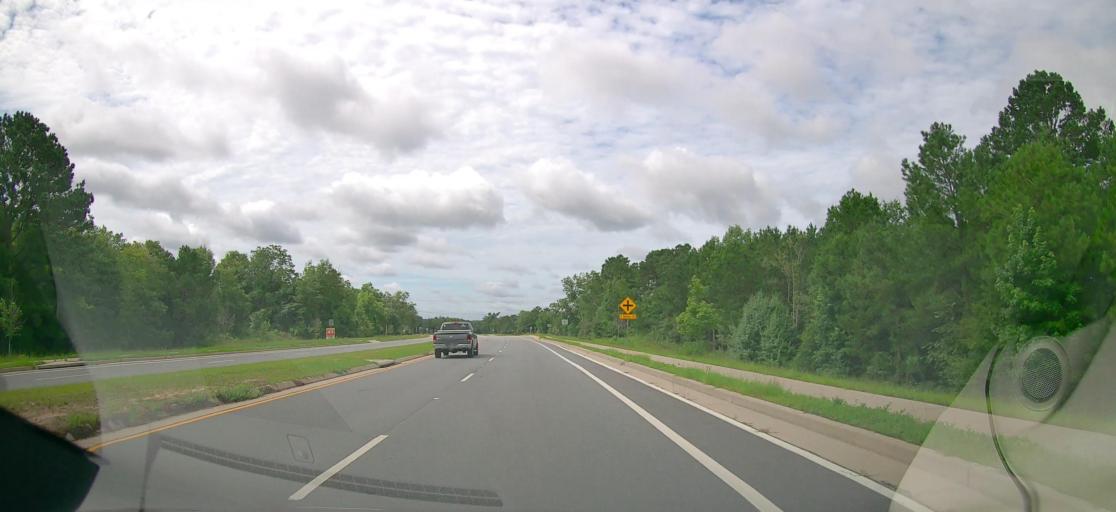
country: US
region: Georgia
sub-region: Houston County
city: Centerville
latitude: 32.7061
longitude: -83.6949
